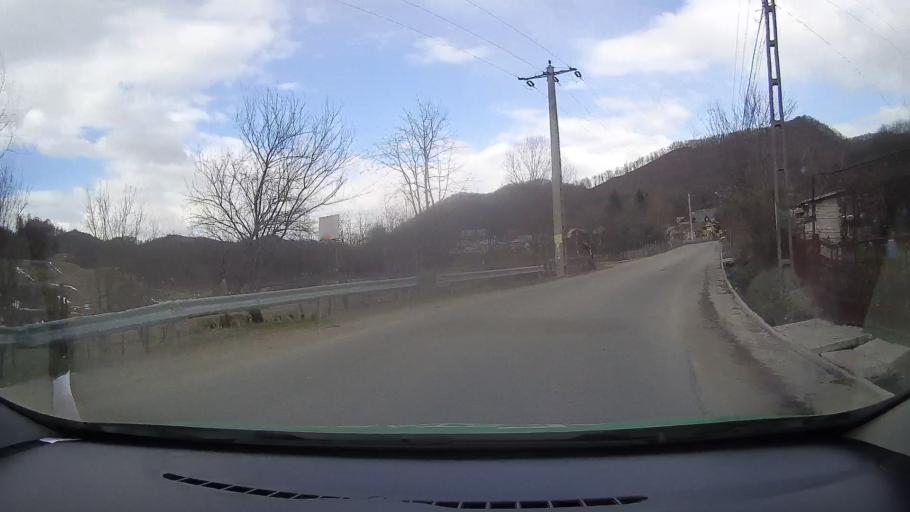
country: RO
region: Dambovita
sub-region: Comuna Varfuri
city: Varfuri
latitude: 45.0758
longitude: 25.5268
